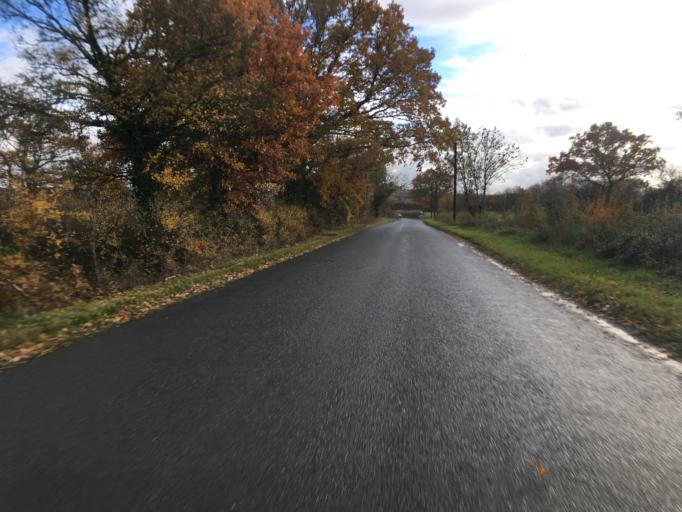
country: GB
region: England
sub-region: South Gloucestershire
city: Siston
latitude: 51.5056
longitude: -2.4614
